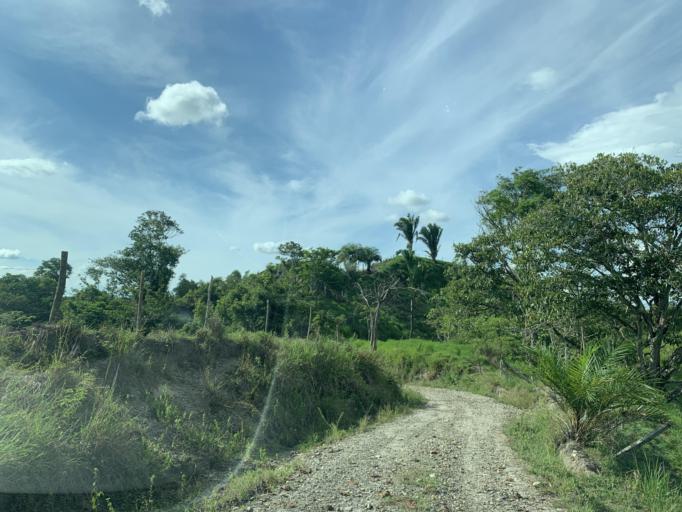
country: CO
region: Boyaca
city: Puerto Boyaca
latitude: 6.0090
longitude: -74.3842
